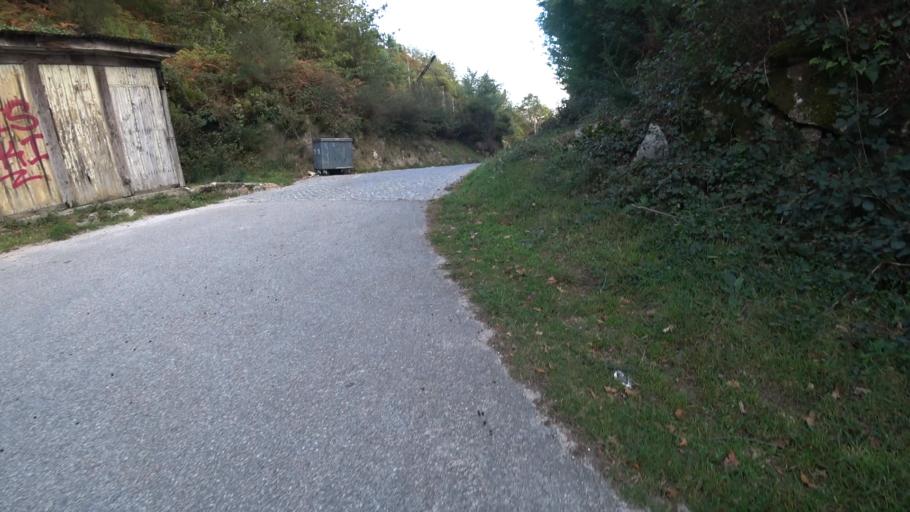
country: PT
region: Braga
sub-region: Terras de Bouro
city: Antas
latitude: 41.7607
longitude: -8.1994
